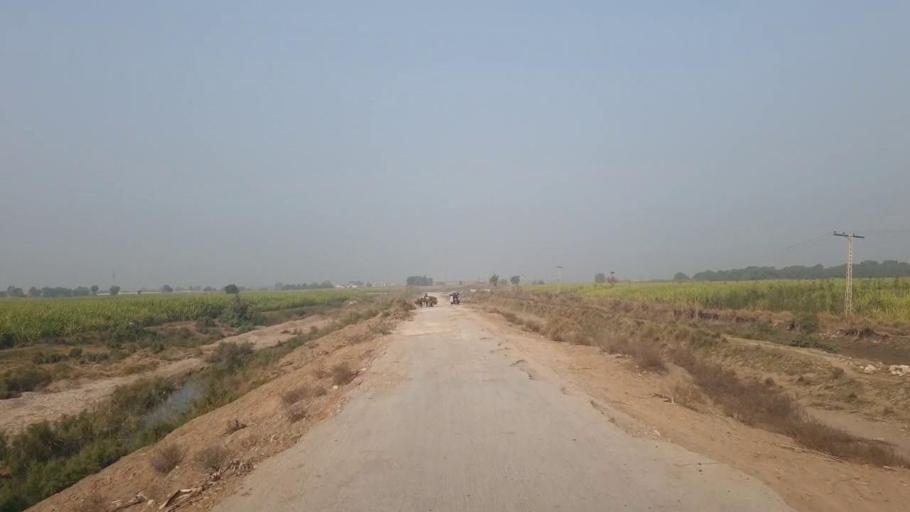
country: PK
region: Sindh
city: Shahdadpur
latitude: 25.8900
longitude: 68.5895
